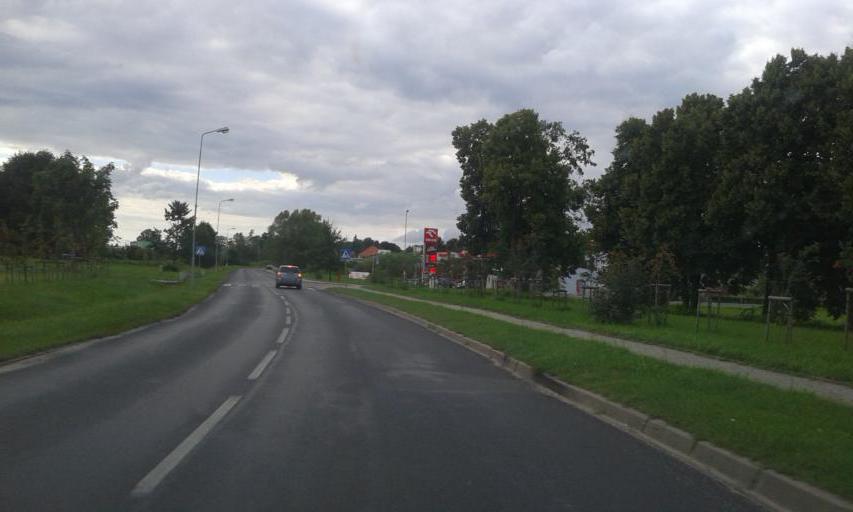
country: PL
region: West Pomeranian Voivodeship
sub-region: Powiat szczecinecki
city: Barwice
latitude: 53.7414
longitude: 16.3518
